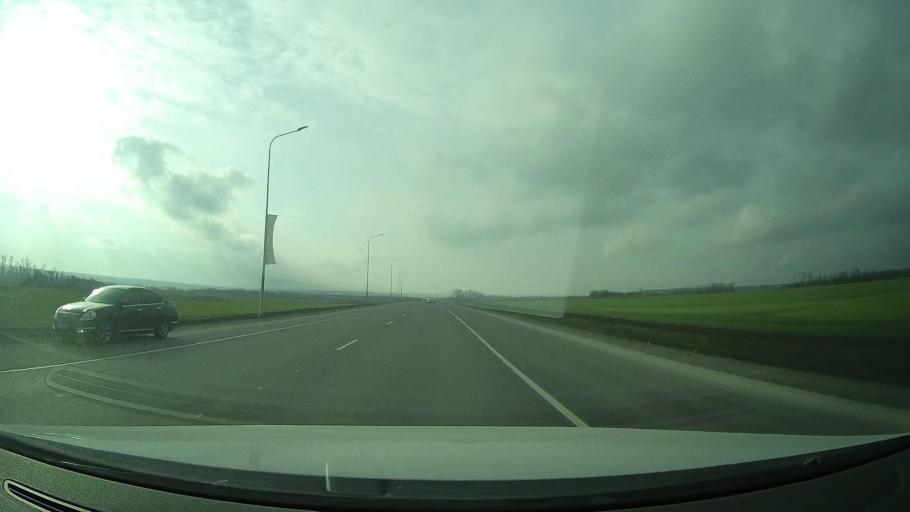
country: RU
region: Rostov
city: Grushevskaya
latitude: 47.4685
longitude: 39.8992
